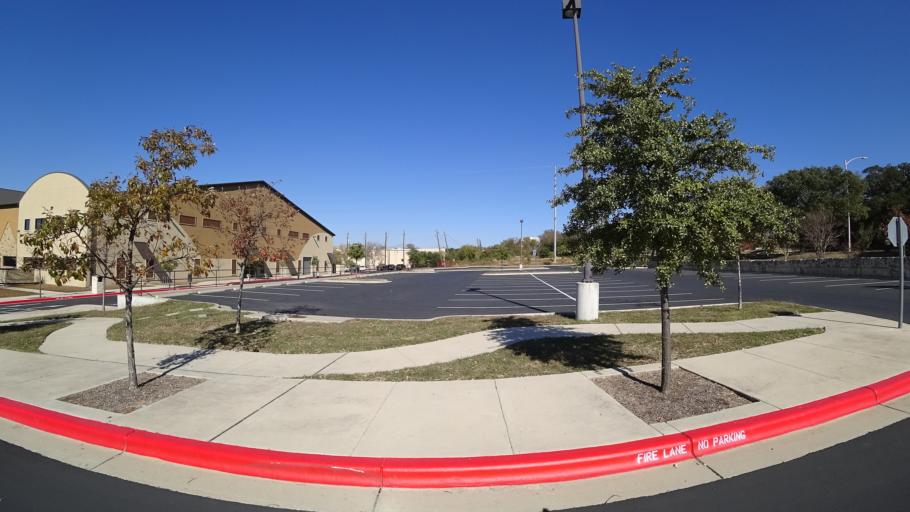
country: US
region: Texas
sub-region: Travis County
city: Wells Branch
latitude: 30.4359
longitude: -97.6971
